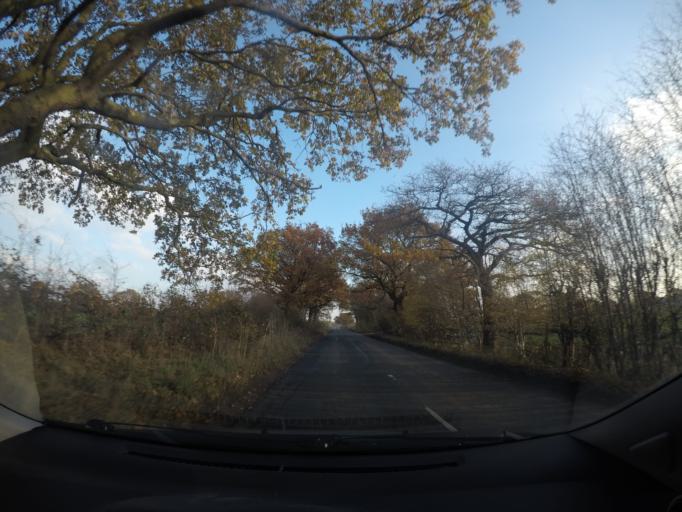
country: GB
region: England
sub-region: City of York
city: Huntington
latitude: 53.9996
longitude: -1.0367
